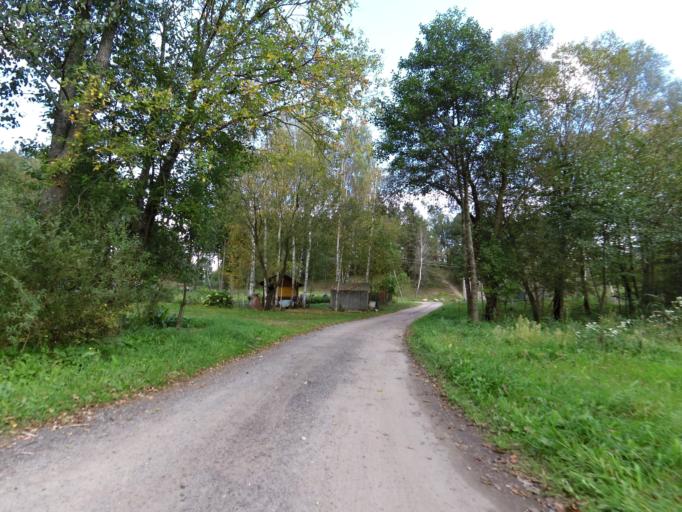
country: LT
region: Vilnius County
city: Pilaite
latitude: 54.7088
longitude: 25.1536
